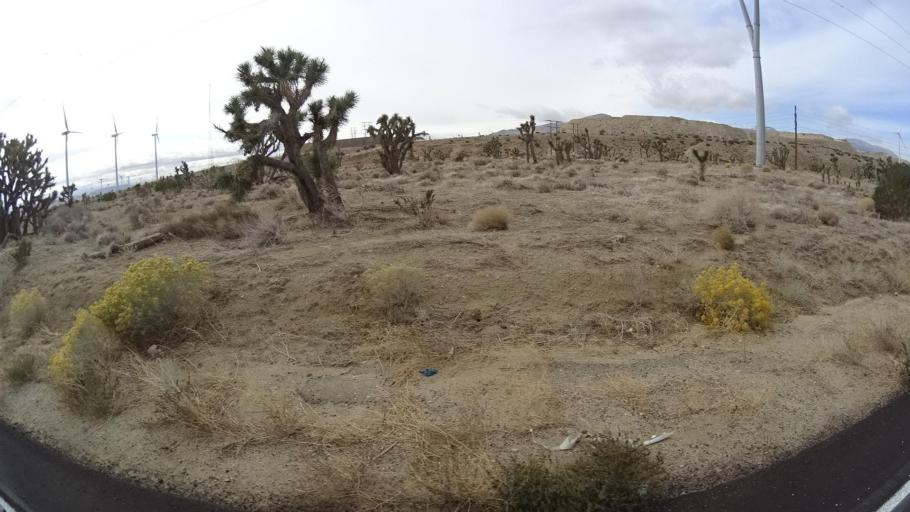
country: US
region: California
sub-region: Kern County
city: Mojave
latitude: 35.0424
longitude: -118.3089
